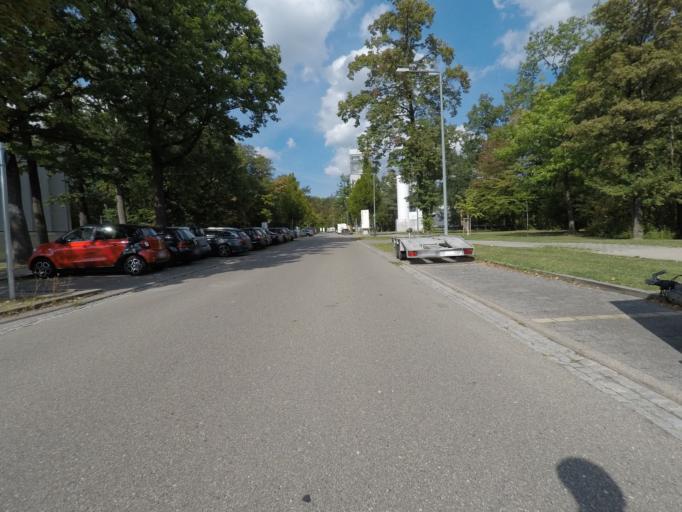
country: DE
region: Baden-Wuerttemberg
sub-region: Regierungsbezirk Stuttgart
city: Gerlingen
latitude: 48.7485
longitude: 9.1101
